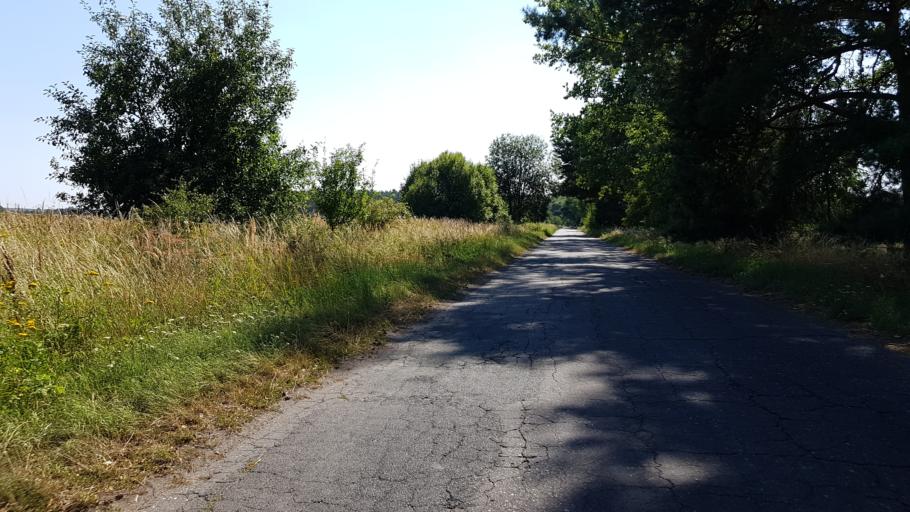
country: PL
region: West Pomeranian Voivodeship
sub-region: Powiat gryfinski
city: Gryfino
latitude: 53.1658
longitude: 14.5313
